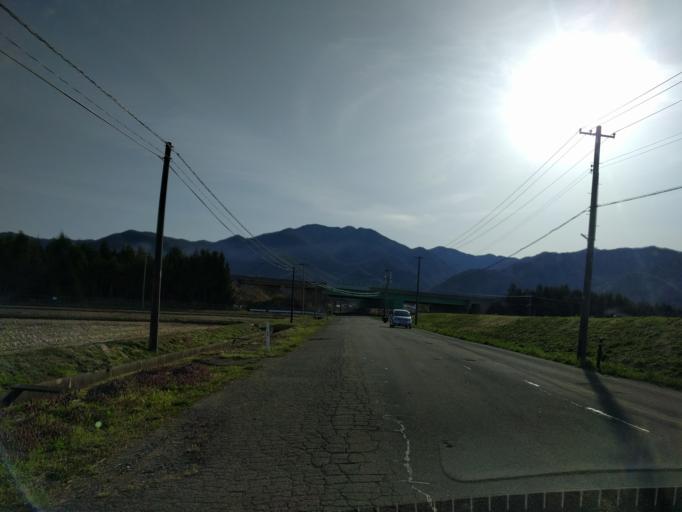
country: JP
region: Fukushima
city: Inawashiro
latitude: 37.5344
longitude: 140.1273
